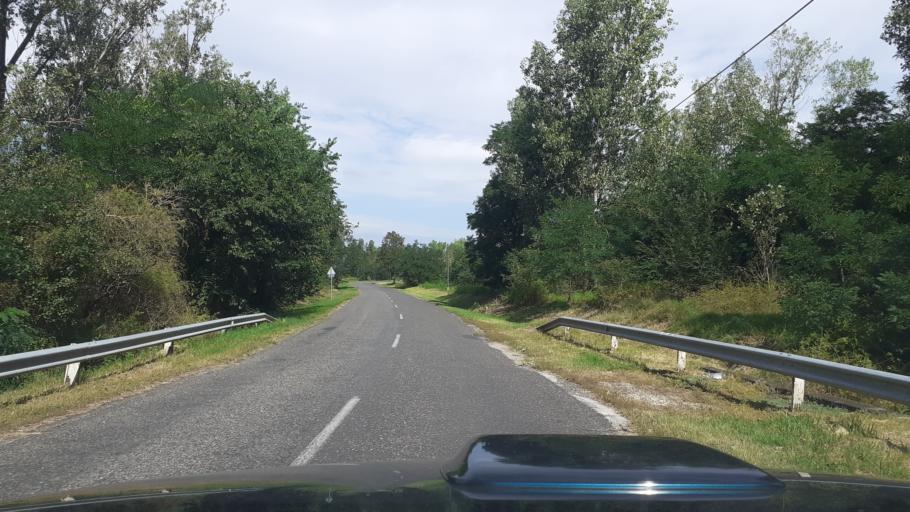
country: HU
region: Fejer
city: Seregelyes
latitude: 47.1298
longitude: 18.5764
